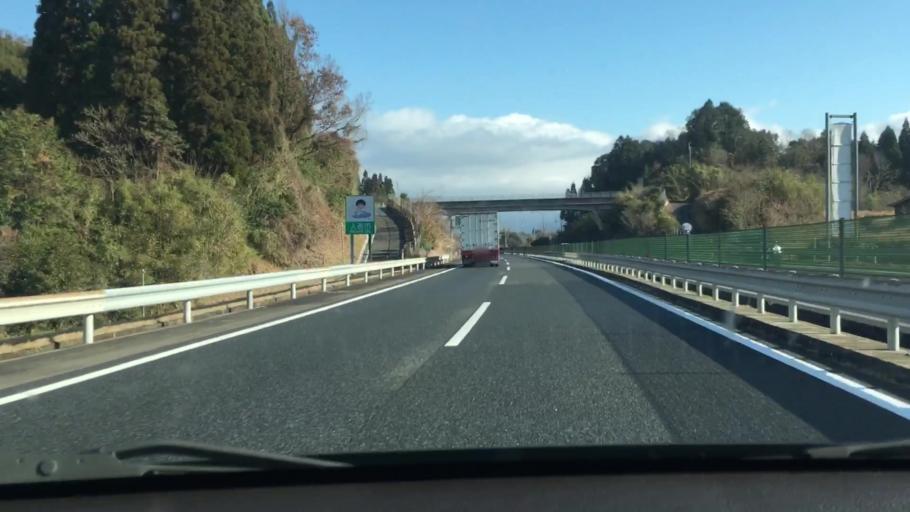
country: JP
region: Kumamoto
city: Hitoyoshi
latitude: 32.2345
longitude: 130.7660
